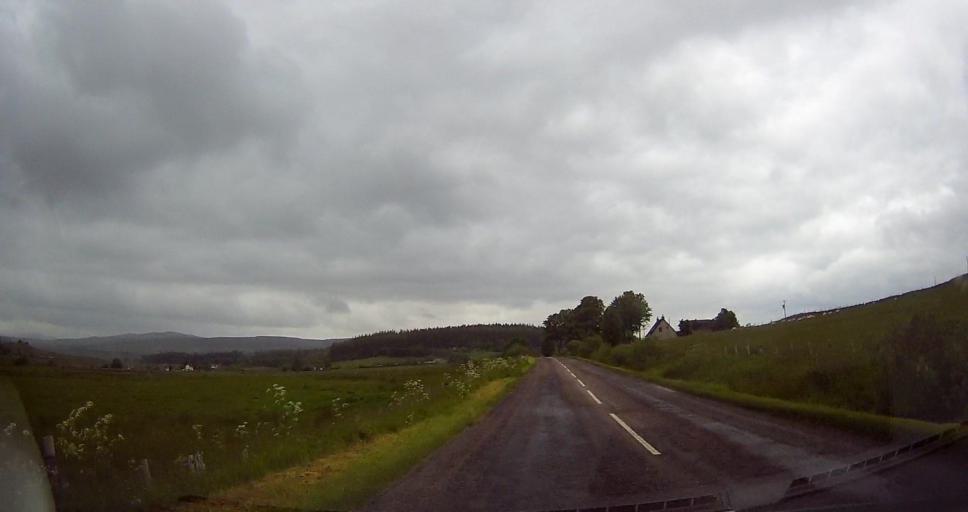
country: GB
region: Scotland
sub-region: Highland
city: Alness
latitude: 58.0186
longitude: -4.3642
